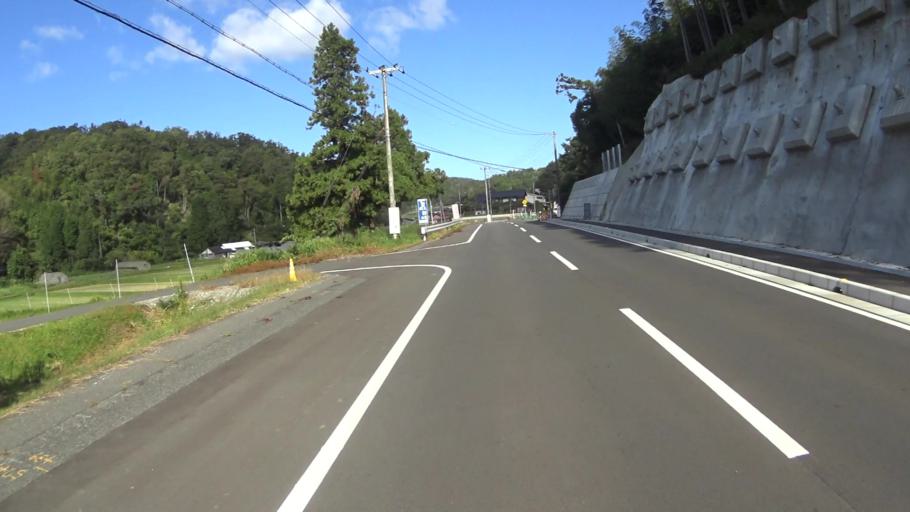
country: JP
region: Kyoto
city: Miyazu
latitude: 35.6079
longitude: 135.1364
